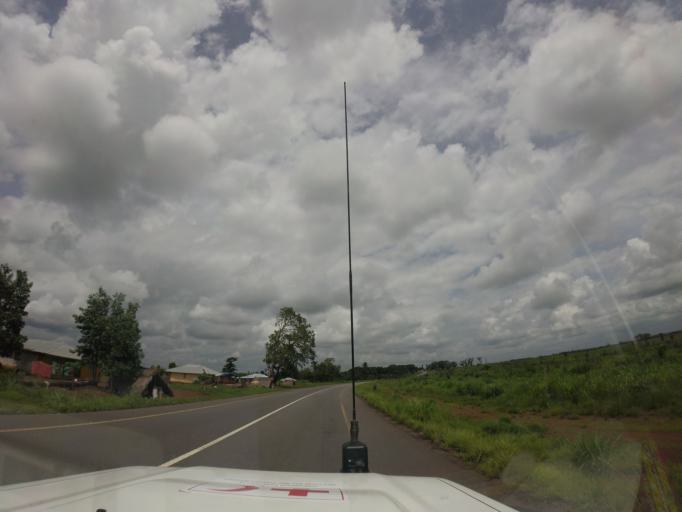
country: SL
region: Northern Province
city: Port Loko
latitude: 8.7382
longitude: -12.7216
